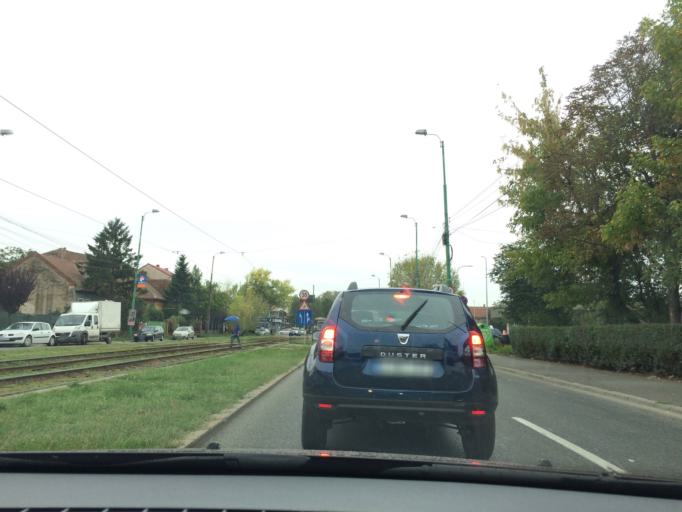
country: RO
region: Timis
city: Timisoara
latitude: 45.7592
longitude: 21.2094
